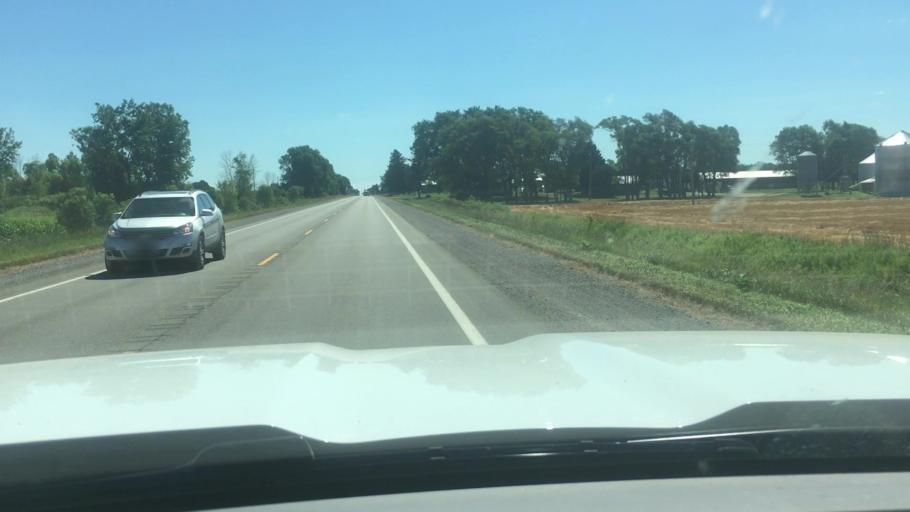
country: US
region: Michigan
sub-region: Montcalm County
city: Carson City
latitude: 43.1766
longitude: -84.8059
